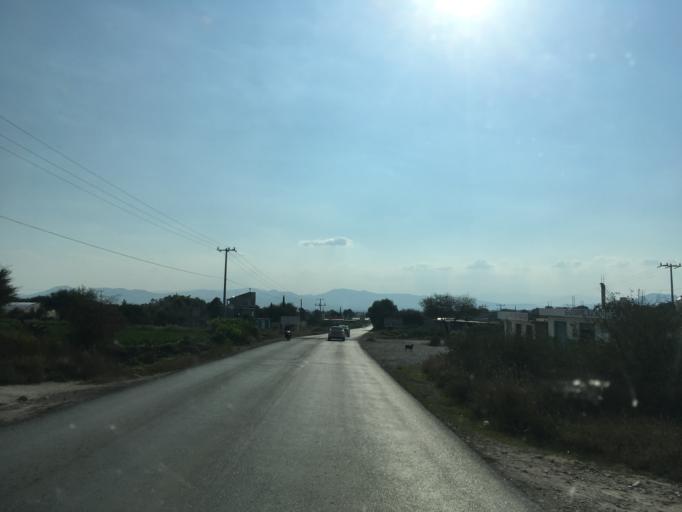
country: MX
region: Hidalgo
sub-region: Ixmiquilpan
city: El Nith
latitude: 20.5576
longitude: -99.1574
